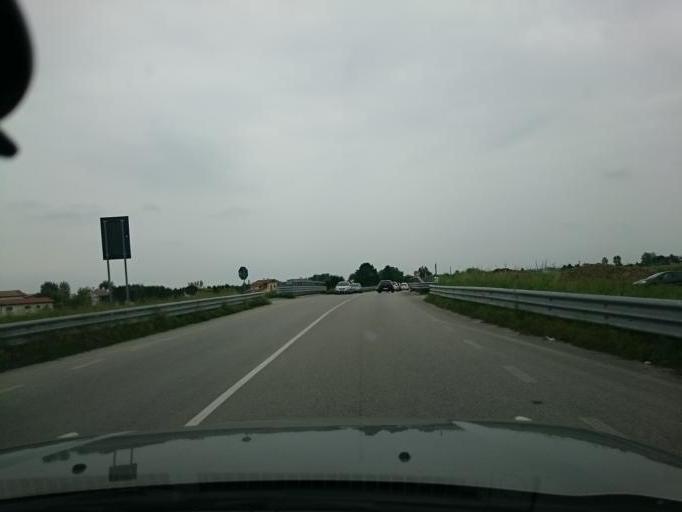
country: IT
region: Veneto
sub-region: Provincia di Padova
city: Montegrotto Terme
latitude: 45.3194
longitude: 11.7957
